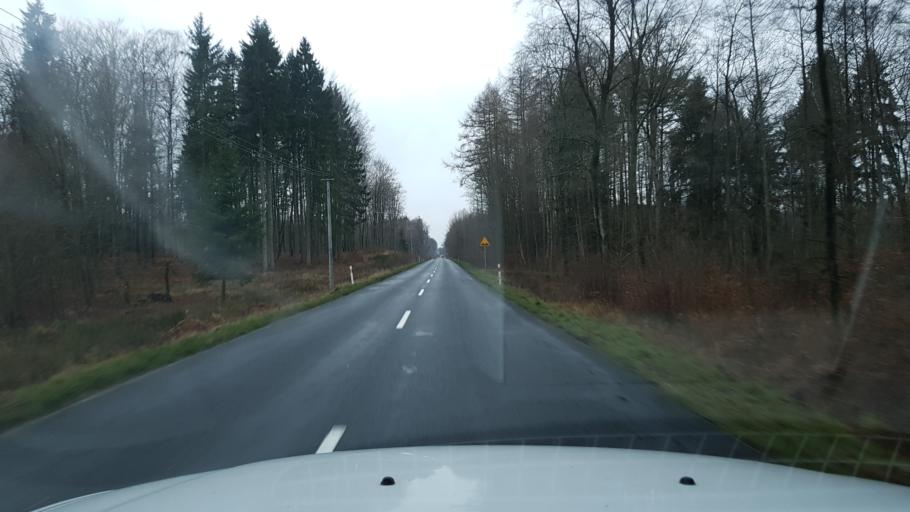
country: PL
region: West Pomeranian Voivodeship
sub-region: Powiat gryficki
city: Trzebiatow
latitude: 54.0560
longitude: 15.3525
